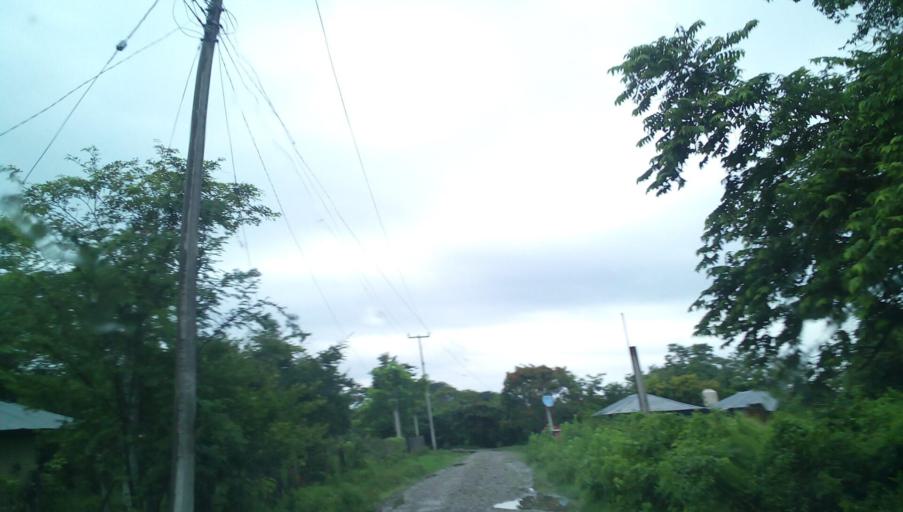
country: MX
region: Veracruz
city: Tempoal de Sanchez
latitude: 21.4185
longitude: -98.4308
